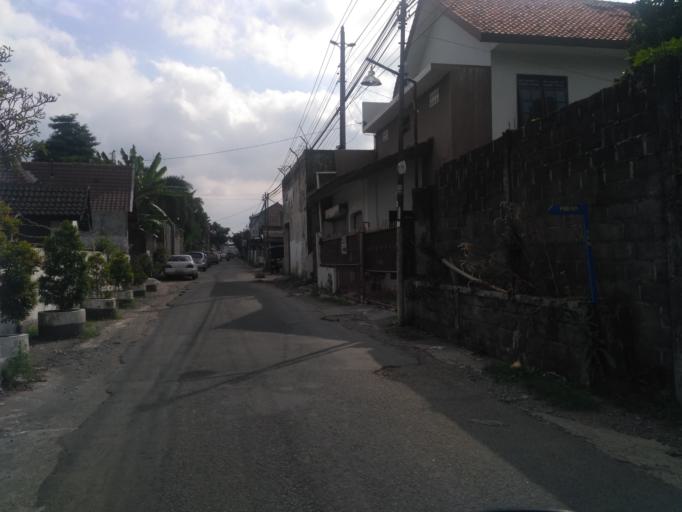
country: ID
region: Daerah Istimewa Yogyakarta
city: Melati
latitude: -7.7529
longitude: 110.3634
